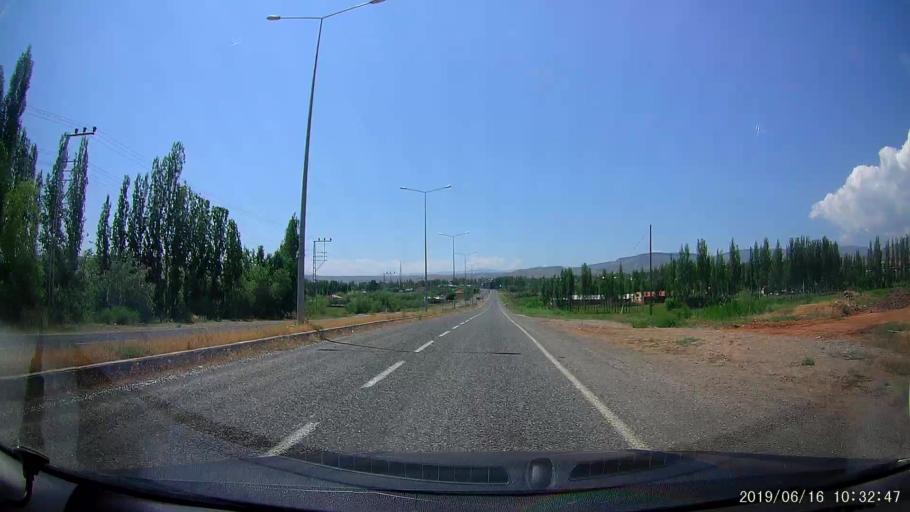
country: TR
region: Igdir
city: Tuzluca
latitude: 40.0467
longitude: 43.6546
